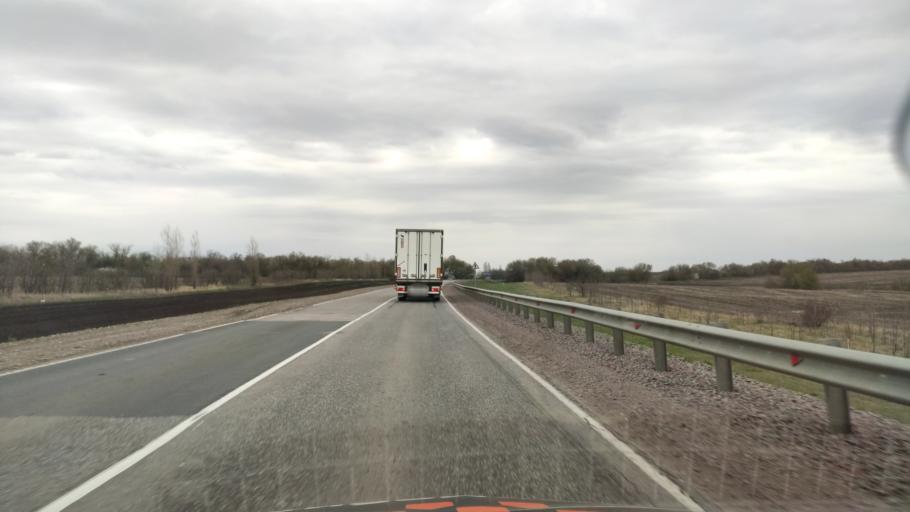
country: RU
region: Voronezj
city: Nizhnedevitsk
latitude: 51.5767
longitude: 38.3183
